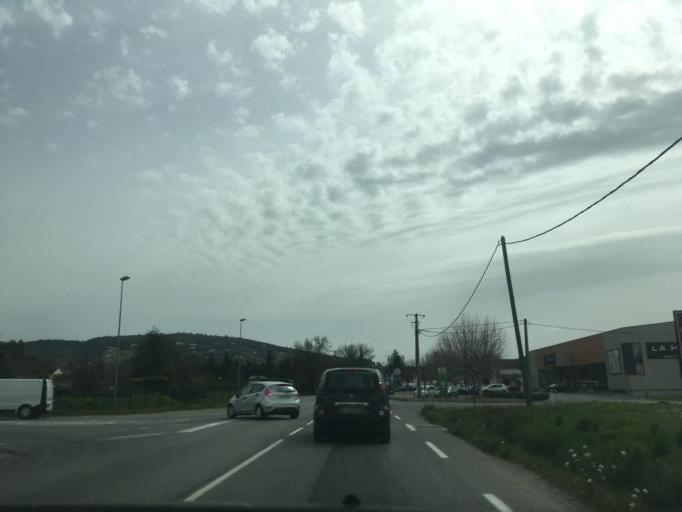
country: FR
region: Provence-Alpes-Cote d'Azur
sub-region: Departement du Var
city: Montauroux
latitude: 43.6051
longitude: 6.7696
